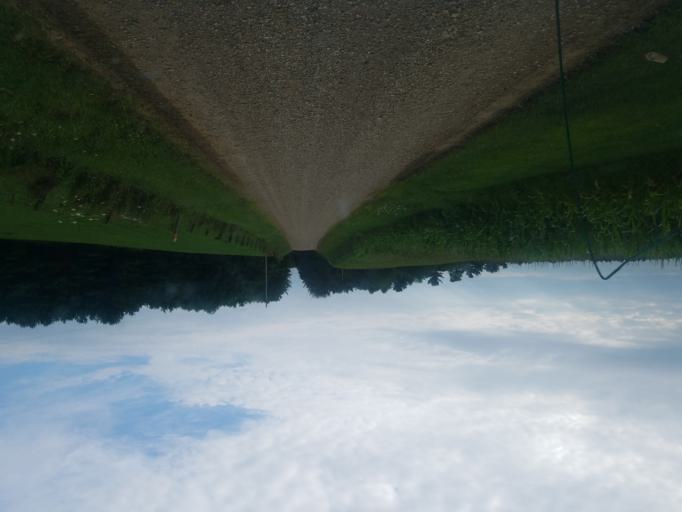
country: US
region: Ohio
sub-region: Knox County
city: Oak Hill
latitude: 40.3319
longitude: -82.1053
